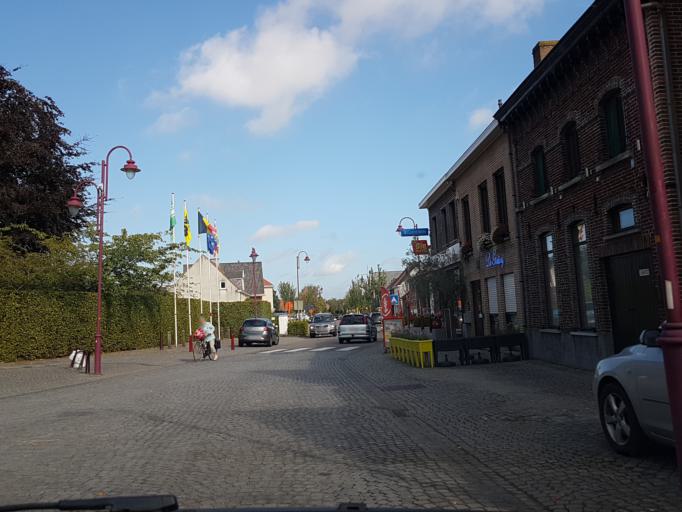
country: BE
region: Flanders
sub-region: Provincie Oost-Vlaanderen
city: Aalter
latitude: 51.0885
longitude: 3.4908
